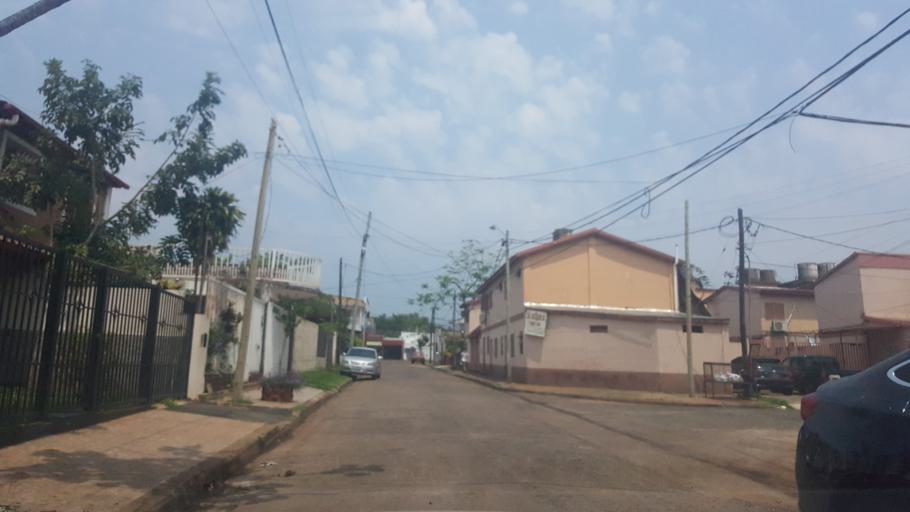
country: AR
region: Misiones
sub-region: Departamento de Capital
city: Posadas
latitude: -27.3680
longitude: -55.9157
